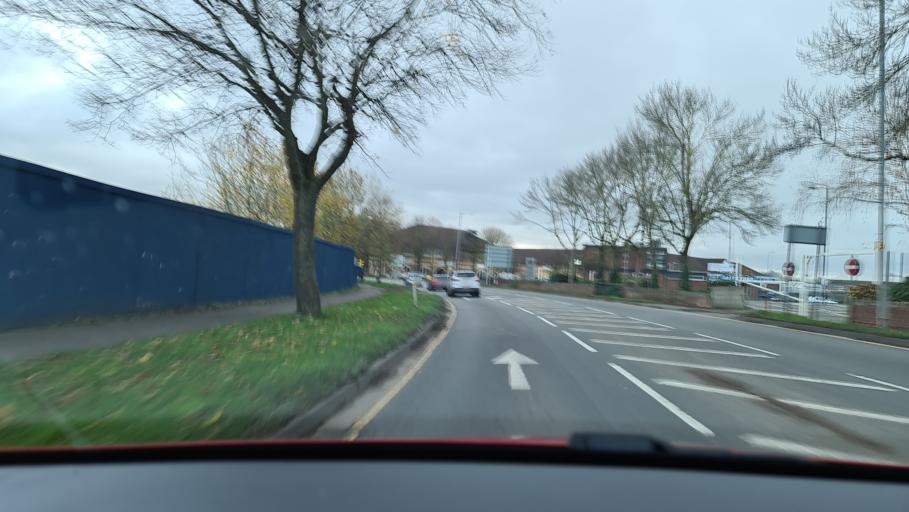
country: GB
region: England
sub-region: Buckinghamshire
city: Aylesbury
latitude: 51.8218
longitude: -0.8261
